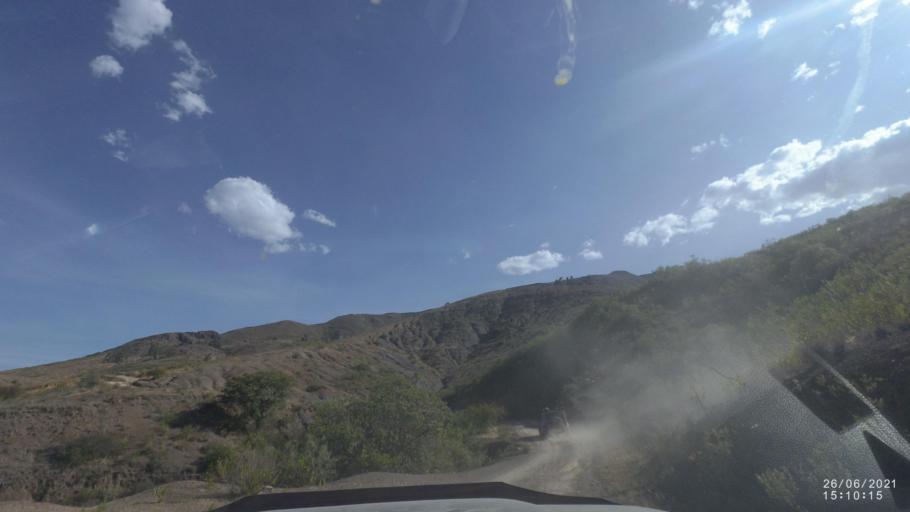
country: BO
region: Cochabamba
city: Mizque
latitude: -17.9532
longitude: -65.6413
